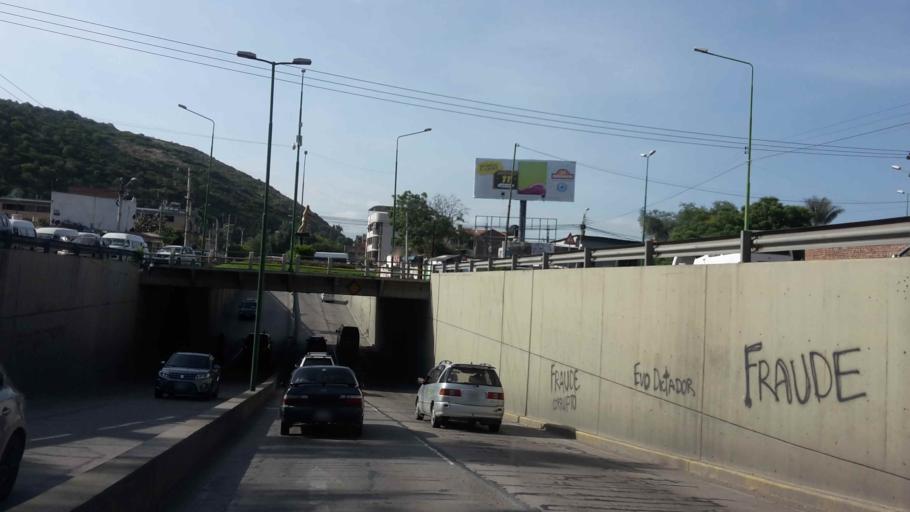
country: BO
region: Cochabamba
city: Cochabamba
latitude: -17.3782
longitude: -66.1422
